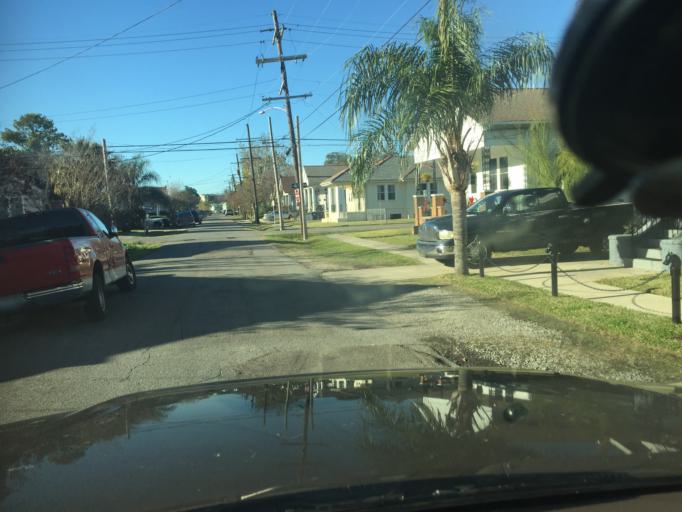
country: US
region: Louisiana
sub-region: Orleans Parish
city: New Orleans
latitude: 29.9843
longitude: -90.0733
